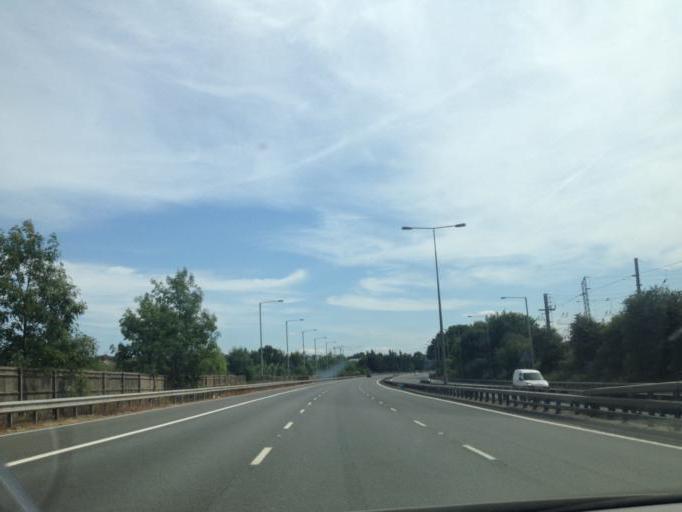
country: GB
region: England
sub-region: Greater London
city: Hendon
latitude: 51.6017
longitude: -0.2377
